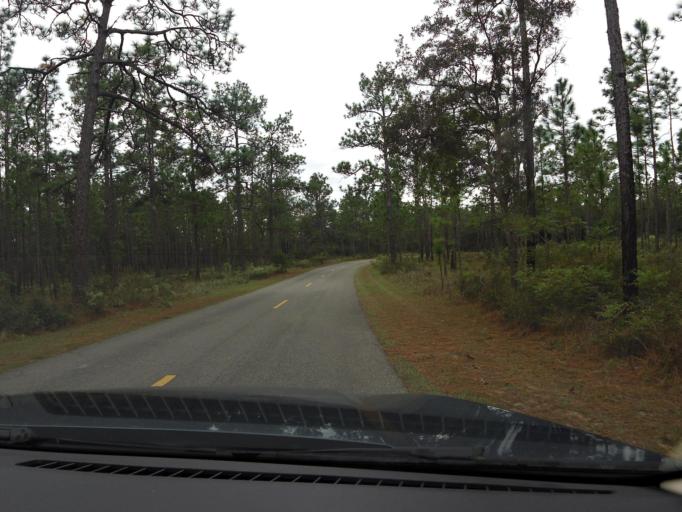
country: US
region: Florida
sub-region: Clay County
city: Keystone Heights
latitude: 29.8439
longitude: -81.9530
